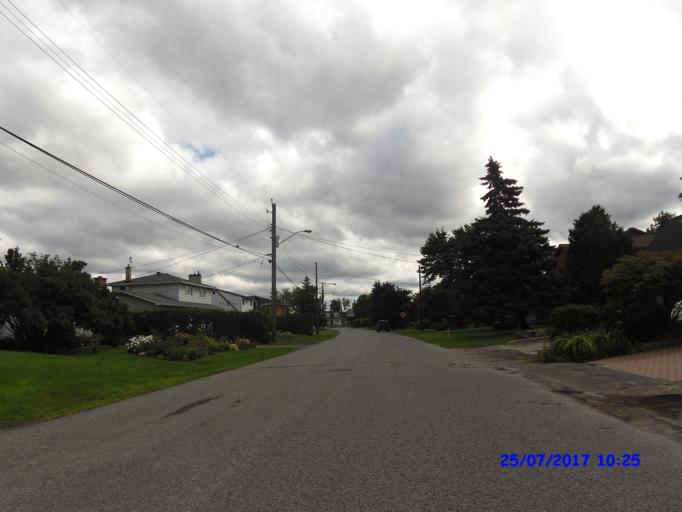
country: CA
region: Ontario
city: Ottawa
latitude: 45.3575
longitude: -75.7036
